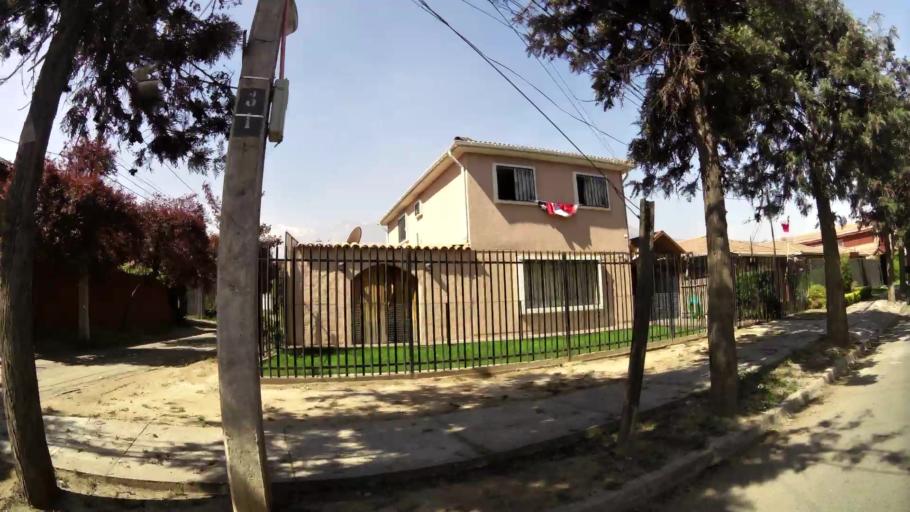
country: CL
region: Santiago Metropolitan
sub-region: Provincia de Santiago
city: Villa Presidente Frei, Nunoa, Santiago, Chile
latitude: -33.5280
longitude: -70.5685
